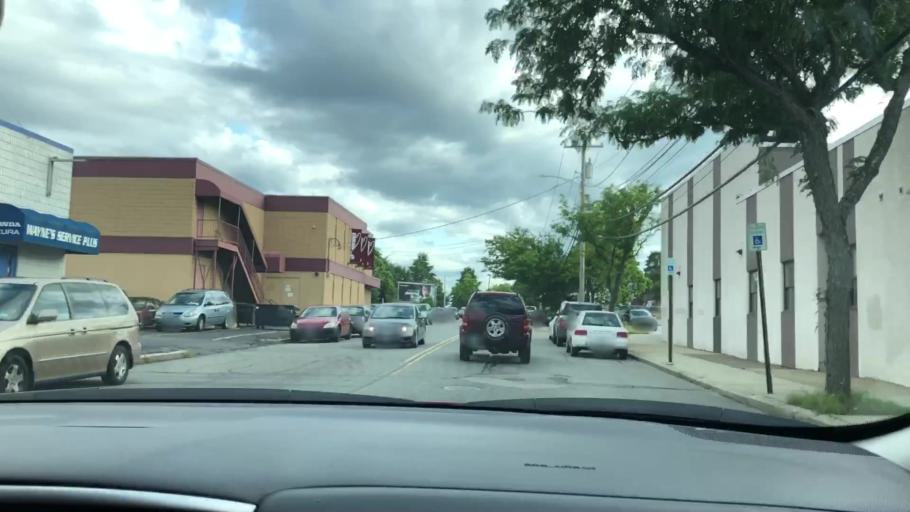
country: US
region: Rhode Island
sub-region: Providence County
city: Providence
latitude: 41.8513
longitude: -71.4132
